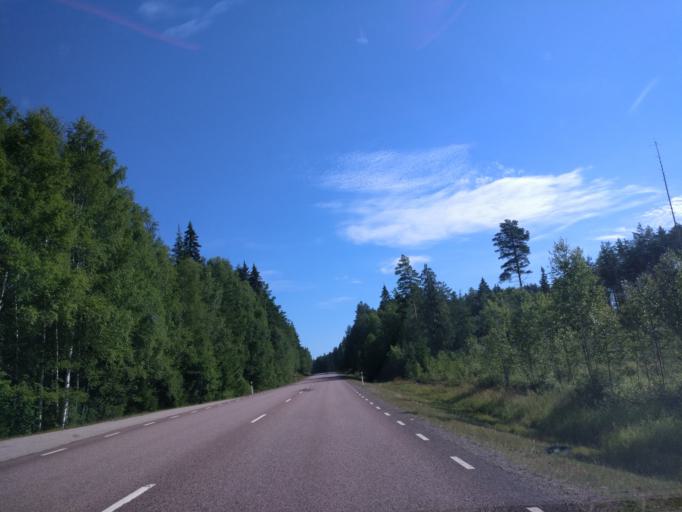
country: SE
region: Vaermland
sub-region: Hagfors Kommun
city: Hagfors
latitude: 60.0581
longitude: 13.7090
